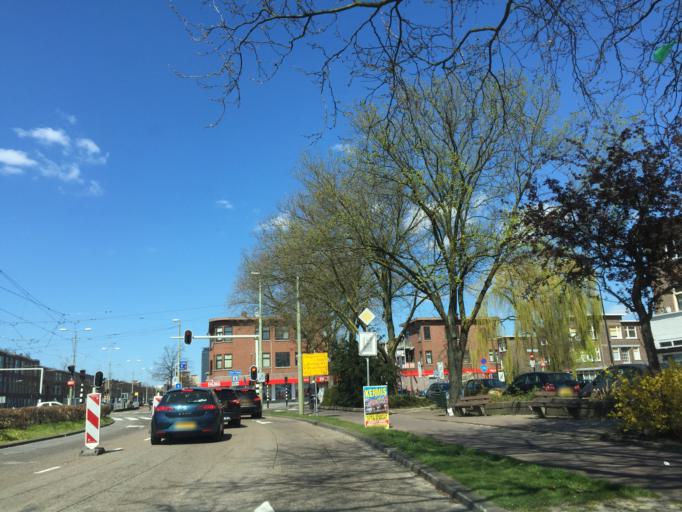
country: NL
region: South Holland
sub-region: Gemeente Rijswijk
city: Rijswijk
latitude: 52.0593
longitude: 4.3356
